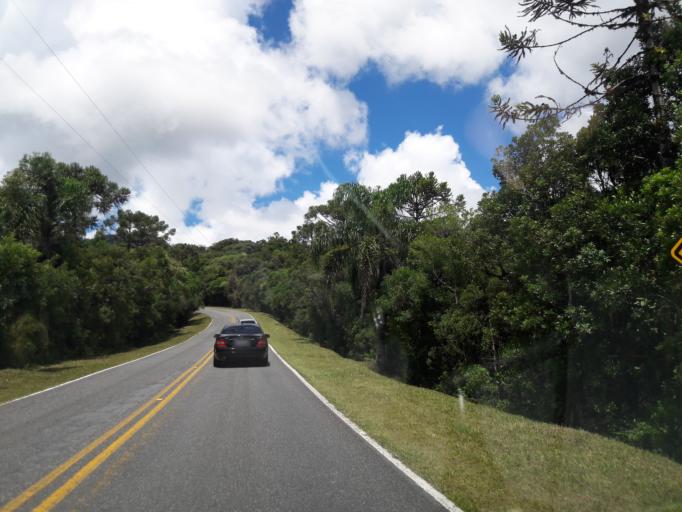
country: BR
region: Parana
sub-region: Campina Grande Do Sul
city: Campina Grande do Sul
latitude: -25.3259
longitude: -48.9186
